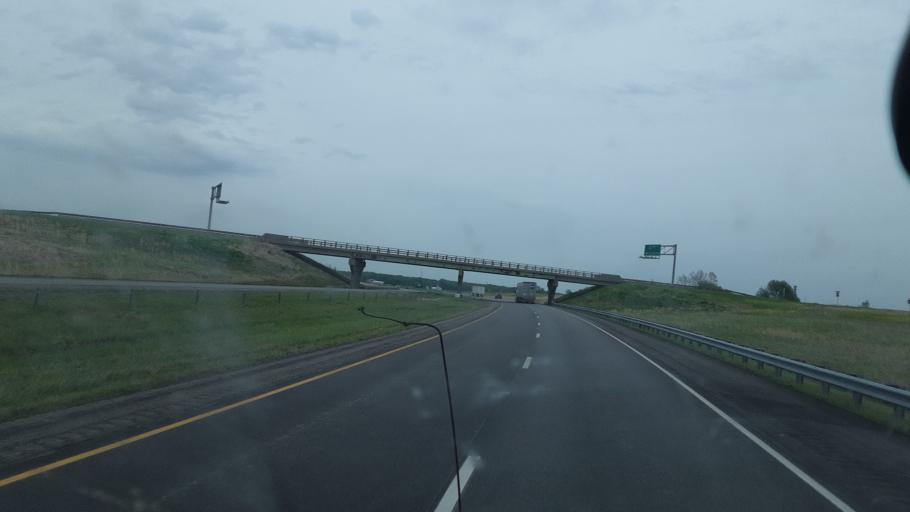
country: US
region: Indiana
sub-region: Posey County
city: Poseyville
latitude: 38.1617
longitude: -87.6862
